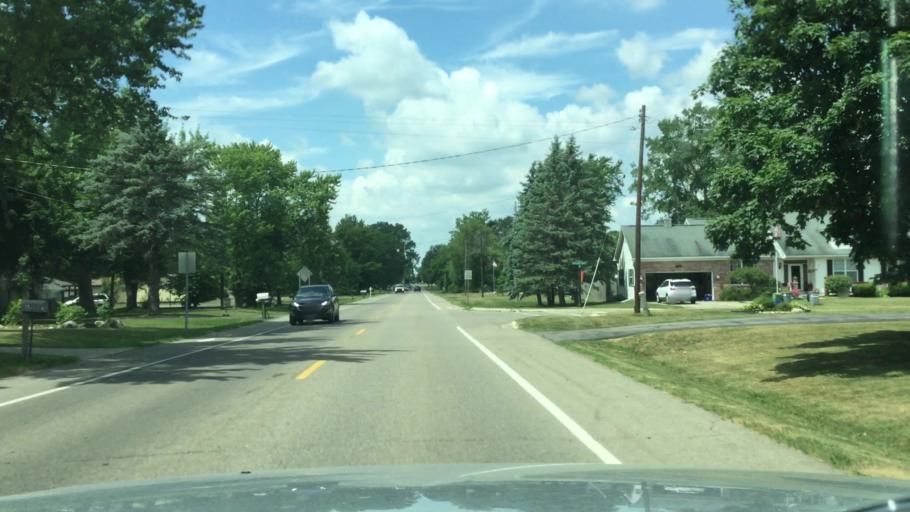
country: US
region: Michigan
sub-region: Genesee County
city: Flushing
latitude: 43.0674
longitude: -83.8183
